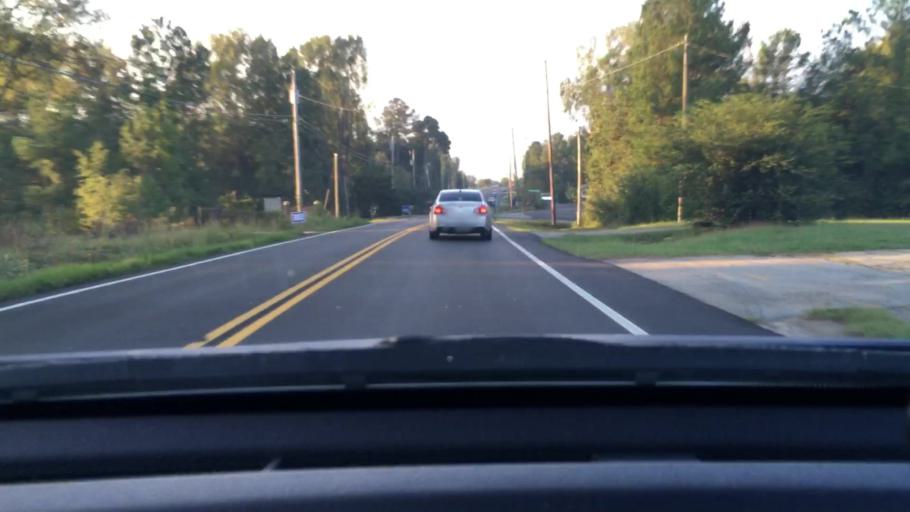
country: US
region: South Carolina
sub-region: Lexington County
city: Irmo
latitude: 34.1015
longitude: -81.1604
